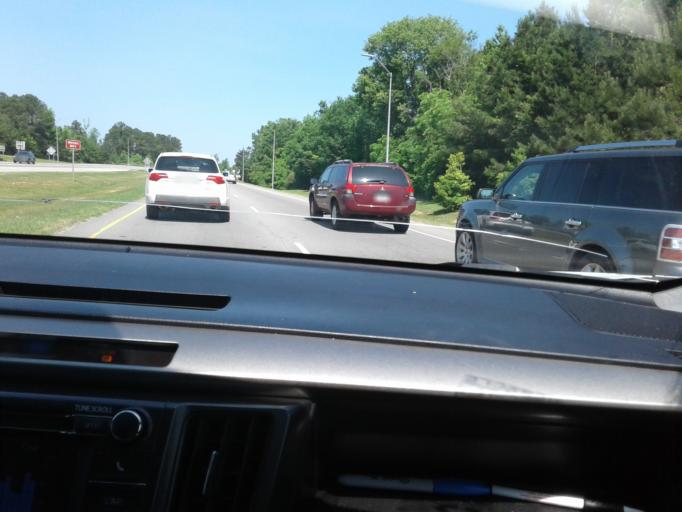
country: US
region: North Carolina
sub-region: Wake County
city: Holly Springs
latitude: 35.6396
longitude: -78.8334
